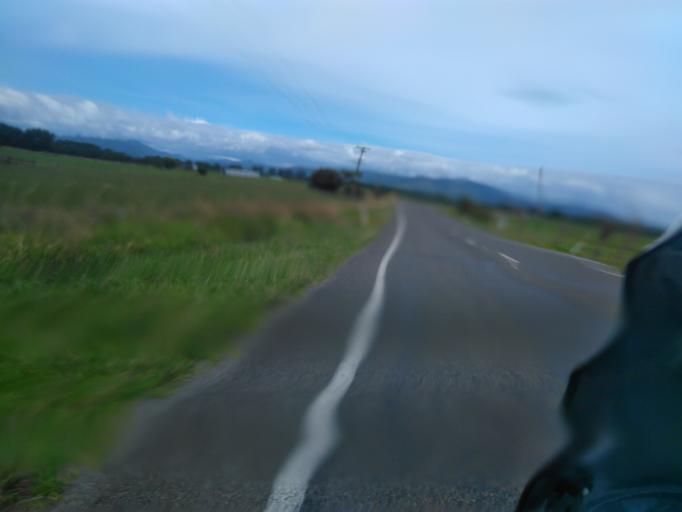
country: NZ
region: Bay of Plenty
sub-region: Opotiki District
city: Opotiki
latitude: -37.9929
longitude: 177.3046
